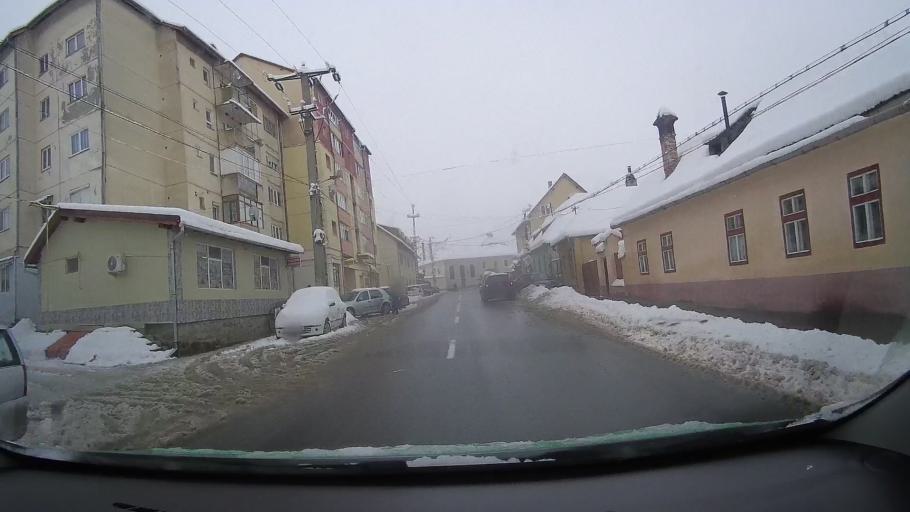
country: RO
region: Sibiu
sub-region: Comuna Orlat
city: Orlat
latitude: 45.7569
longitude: 23.9662
